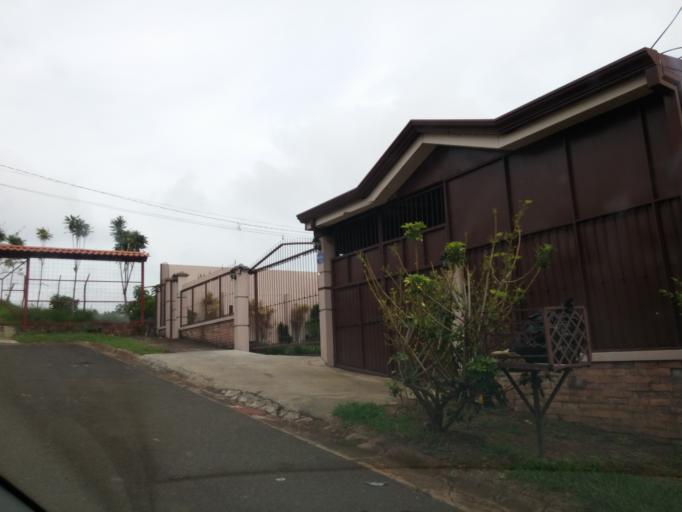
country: CR
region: Heredia
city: Mercedes
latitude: 10.0194
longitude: -84.1507
